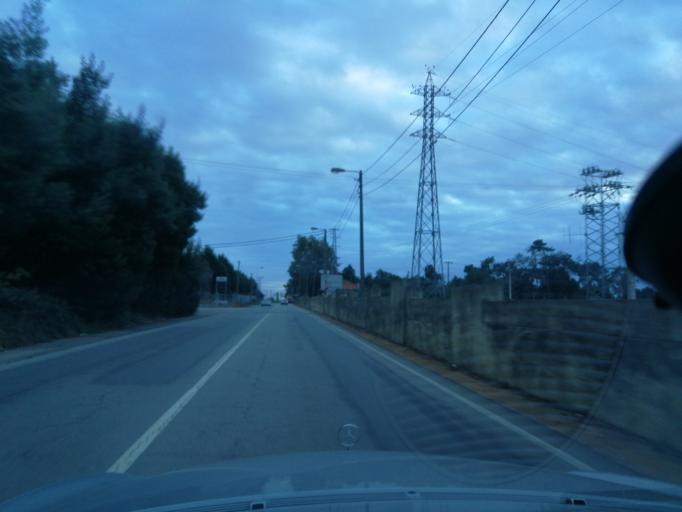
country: PT
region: Aveiro
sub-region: Estarreja
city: Beduido
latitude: 40.7770
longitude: -8.5675
